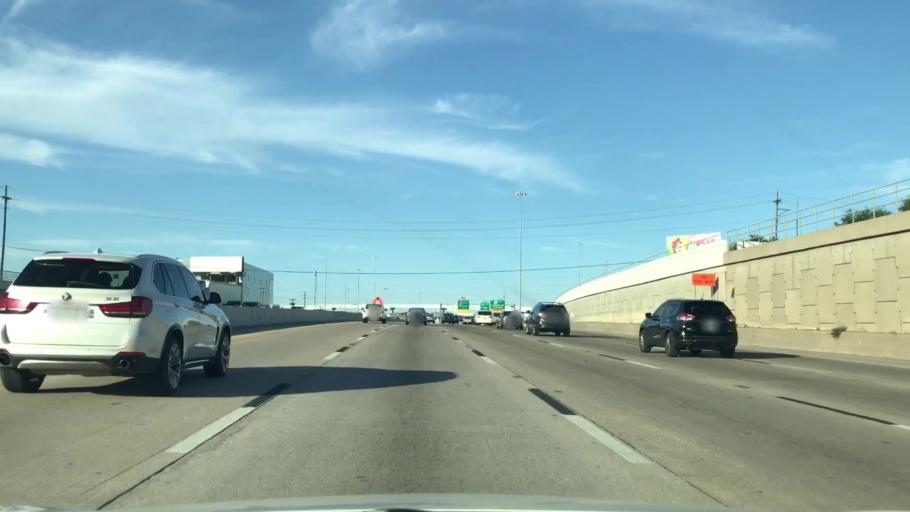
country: US
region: Texas
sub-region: Tarrant County
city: Fort Worth
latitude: 32.7385
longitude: -97.3204
